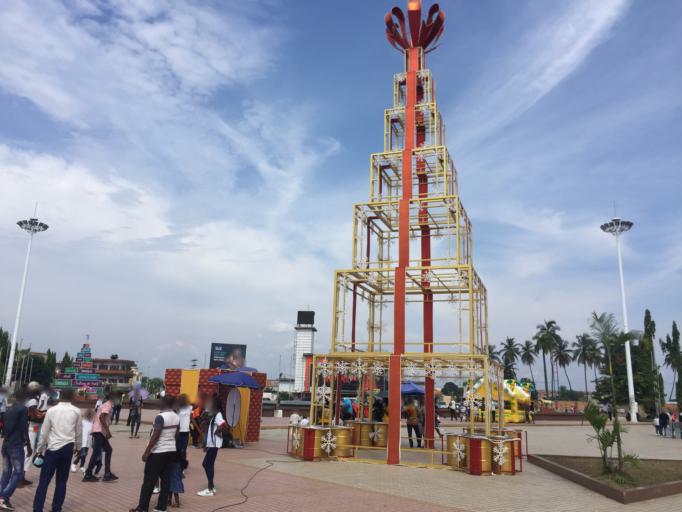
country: CD
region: Kinshasa
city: Kinshasa
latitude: -4.3016
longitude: 15.3167
